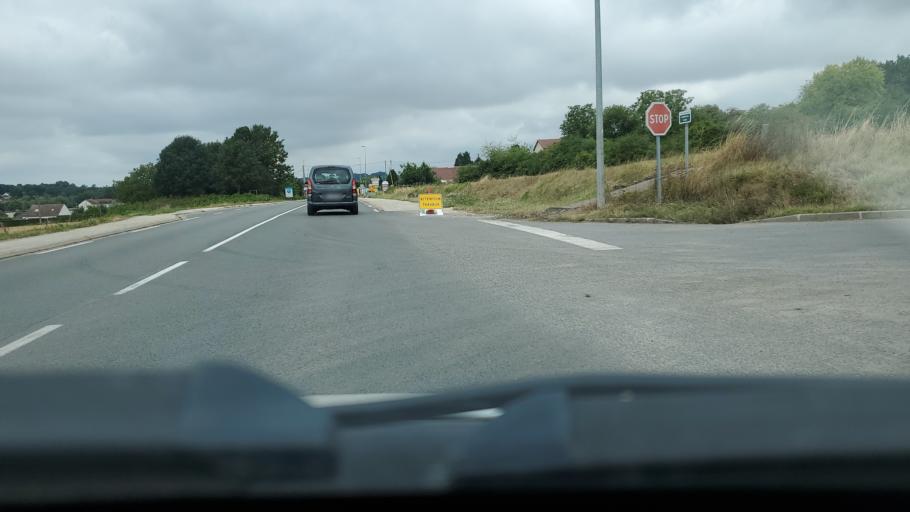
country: FR
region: Ile-de-France
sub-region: Departement de Seine-et-Marne
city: Mouroux
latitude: 48.8169
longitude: 3.0587
